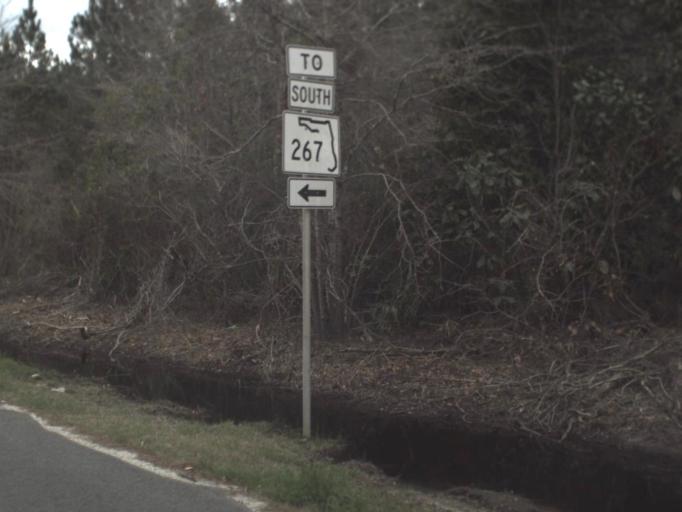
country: US
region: Florida
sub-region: Gadsden County
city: Quincy
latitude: 30.3897
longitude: -84.6837
